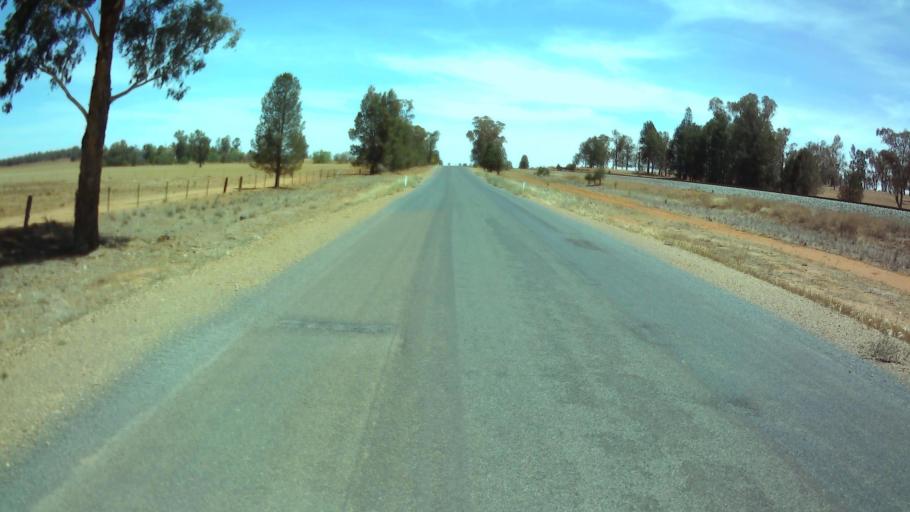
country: AU
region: New South Wales
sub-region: Weddin
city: Grenfell
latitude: -33.7698
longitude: 147.7574
